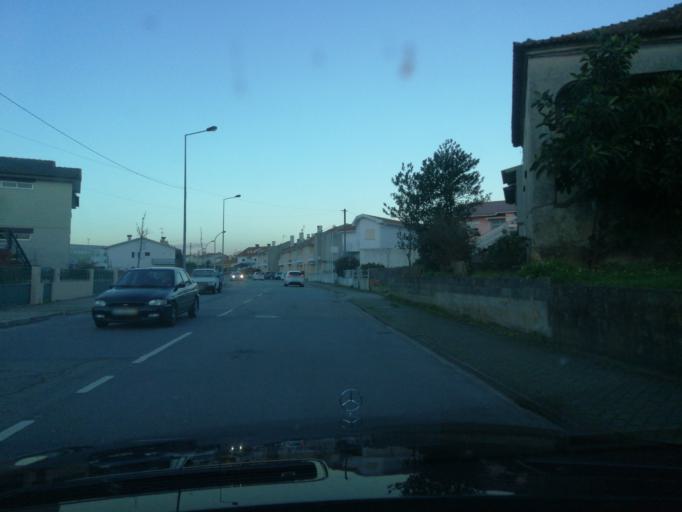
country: PT
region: Aveiro
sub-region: Estarreja
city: Estarreja
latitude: 40.7590
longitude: -8.5735
